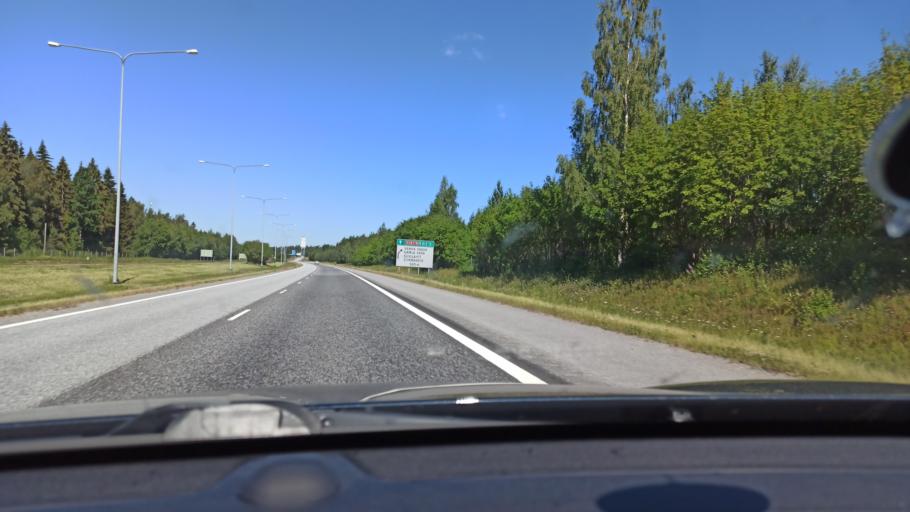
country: FI
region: Ostrobothnia
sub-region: Vaasa
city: Ristinummi
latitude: 63.0627
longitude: 21.7076
